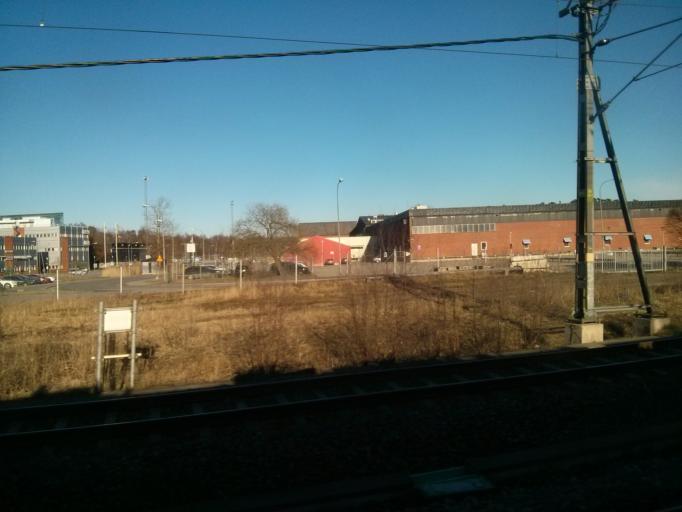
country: SE
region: Stockholm
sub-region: Upplands Vasby Kommun
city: Upplands Vaesby
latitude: 59.4785
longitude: 17.9127
